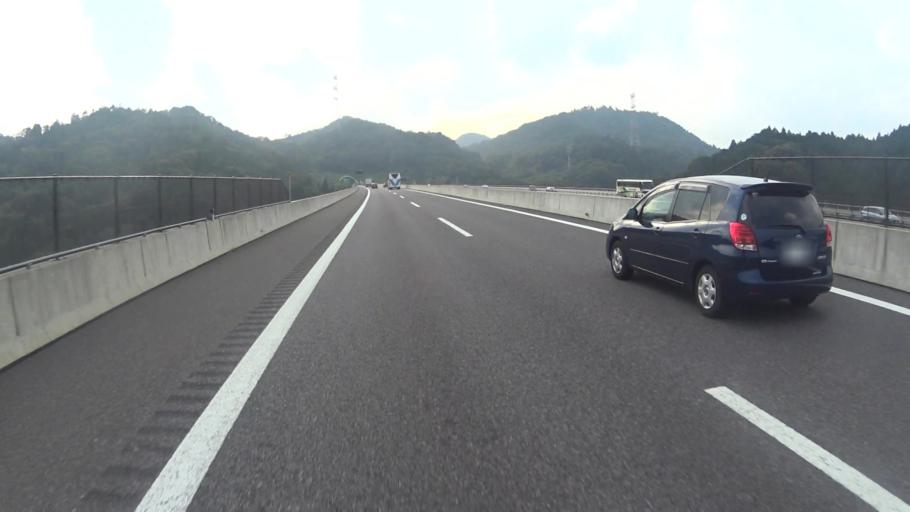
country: JP
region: Shiga Prefecture
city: Minakuchicho-matoba
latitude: 34.9191
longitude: 136.1403
